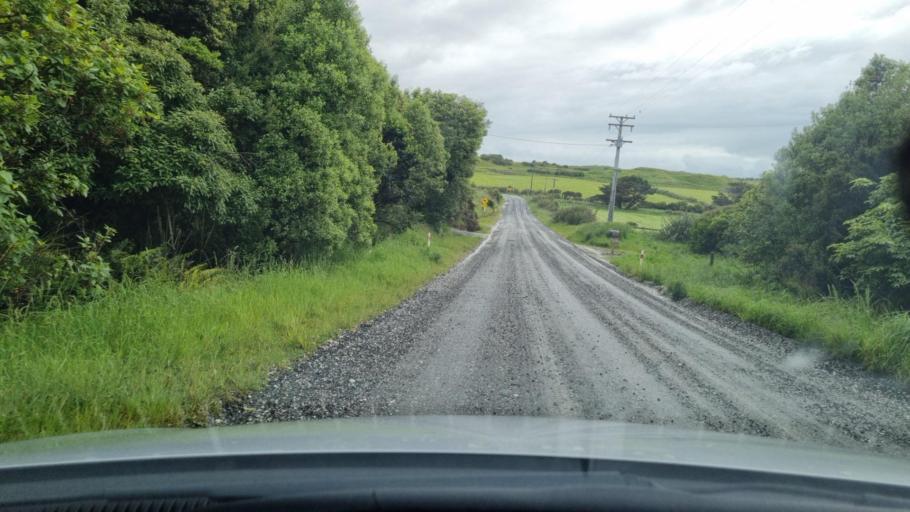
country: NZ
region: Southland
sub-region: Invercargill City
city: Bluff
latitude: -46.5224
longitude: 168.2717
